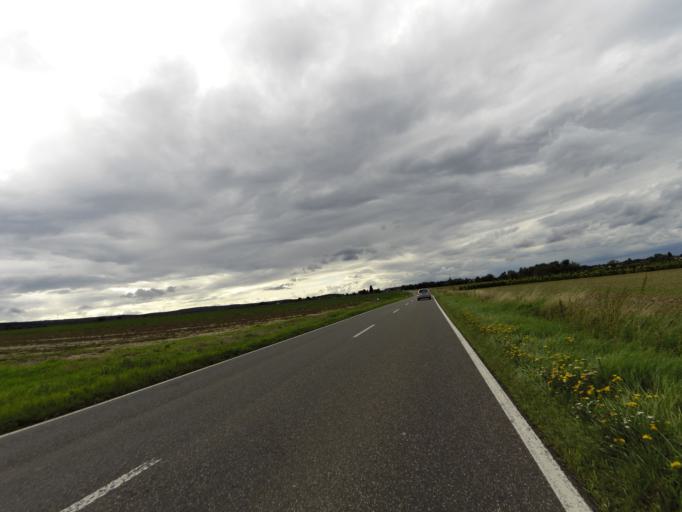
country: DE
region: North Rhine-Westphalia
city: Meckenheim
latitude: 50.5806
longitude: 7.0447
